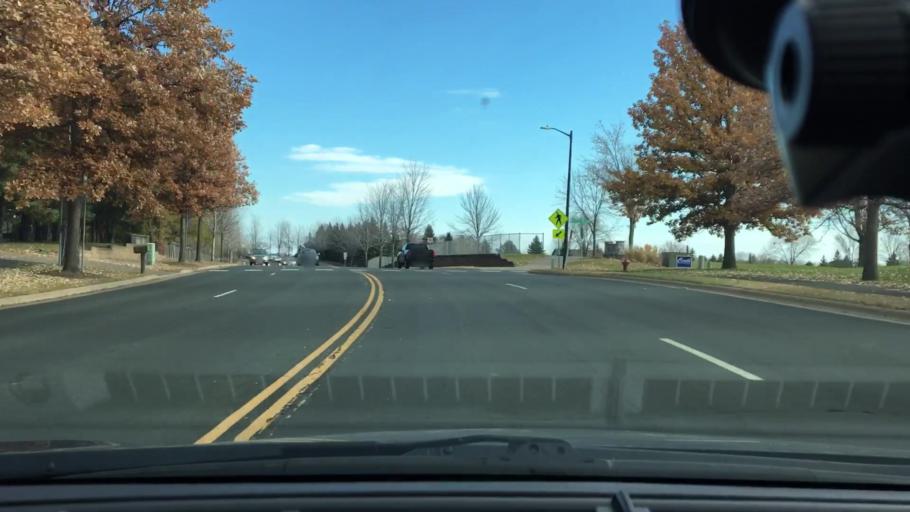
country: US
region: Minnesota
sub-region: Hennepin County
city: Maple Grove
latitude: 45.1030
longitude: -93.4756
